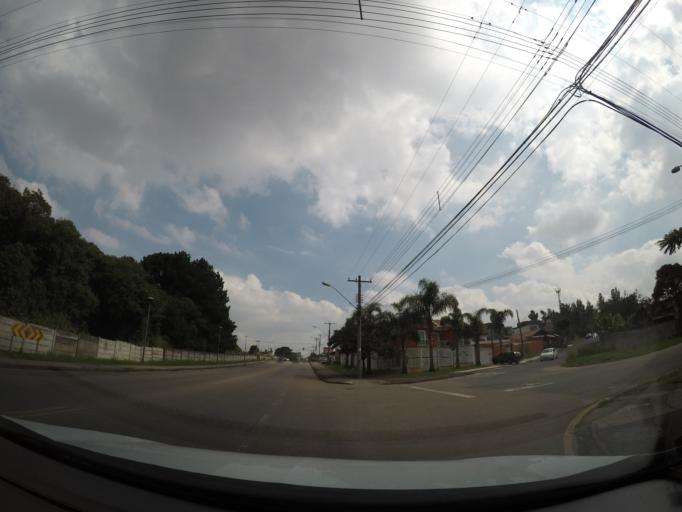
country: BR
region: Parana
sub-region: Sao Jose Dos Pinhais
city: Sao Jose dos Pinhais
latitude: -25.5067
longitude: -49.2459
